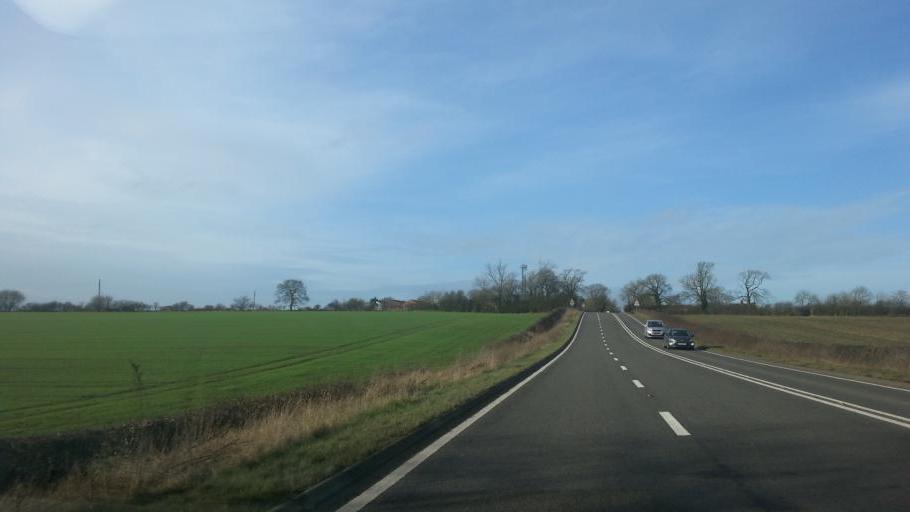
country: GB
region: England
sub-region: Leicestershire
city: Houghton on the Hill
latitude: 52.6080
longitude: -0.8835
